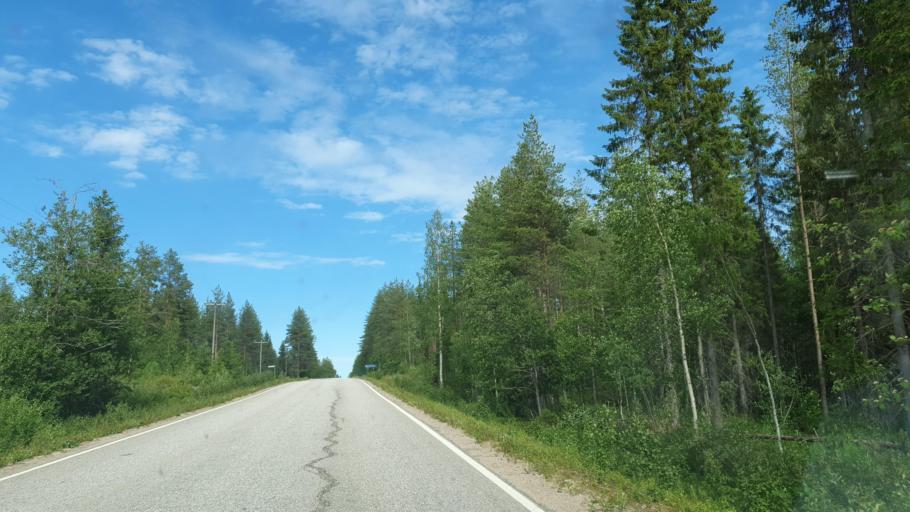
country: FI
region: Kainuu
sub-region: Kehys-Kainuu
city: Suomussalmi
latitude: 64.5846
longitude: 29.0566
